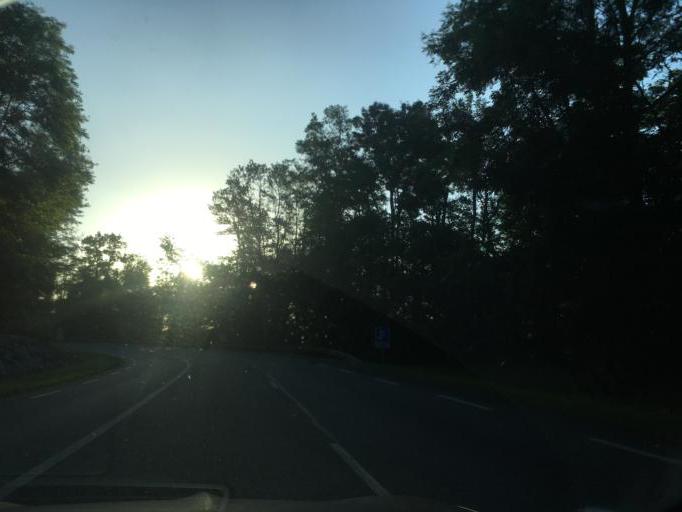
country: FR
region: Midi-Pyrenees
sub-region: Departement des Hautes-Pyrenees
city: Ibos
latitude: 43.2401
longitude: -0.0249
